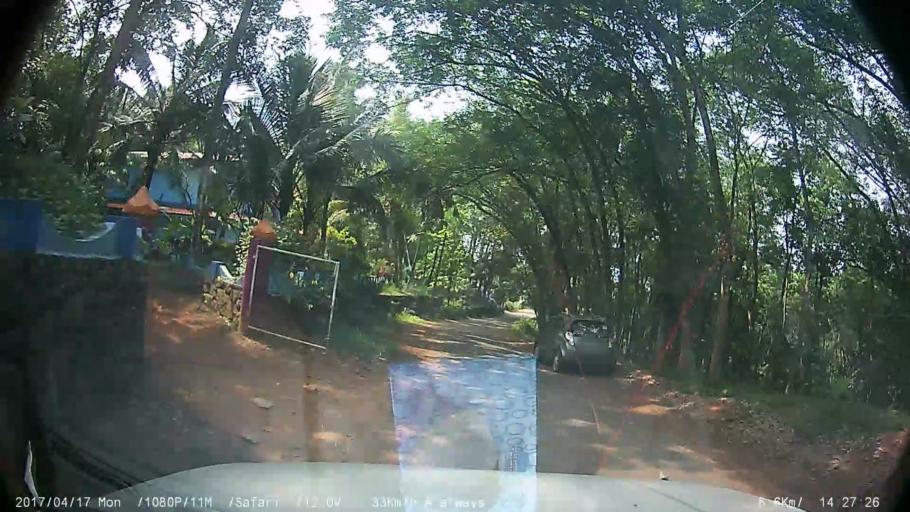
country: IN
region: Kerala
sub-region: Ernakulam
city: Piravam
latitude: 9.7970
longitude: 76.5544
